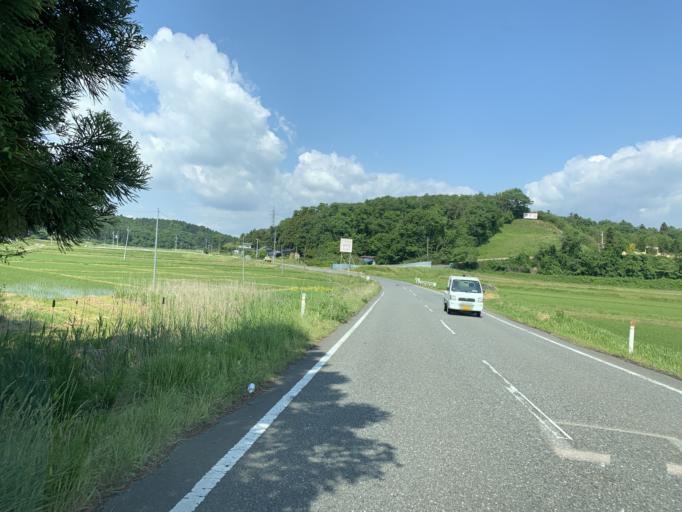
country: JP
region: Iwate
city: Ichinoseki
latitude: 38.7962
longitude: 141.0459
